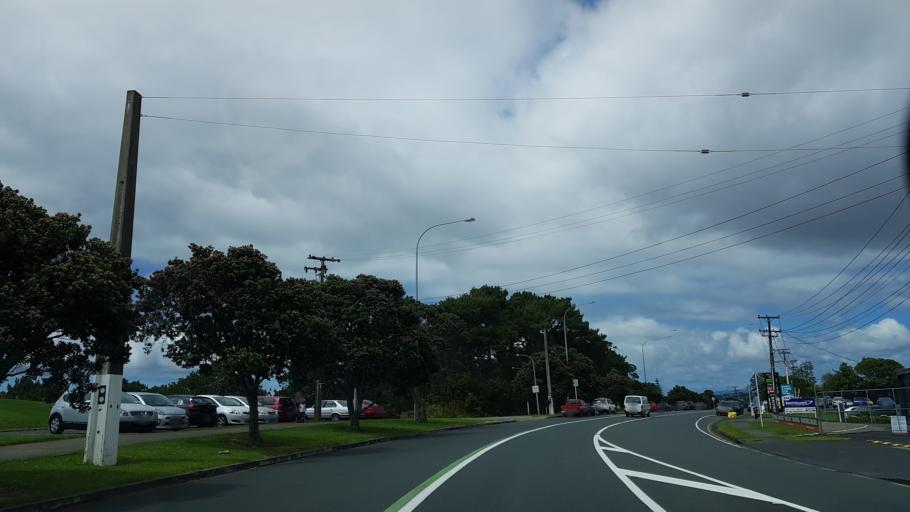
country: NZ
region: Auckland
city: Murrays Bay
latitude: -36.7579
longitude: 174.7509
